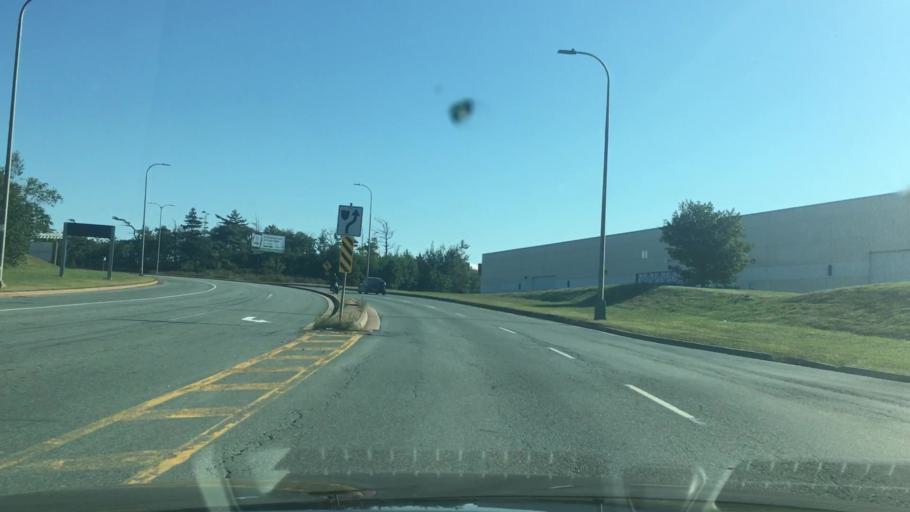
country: CA
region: Nova Scotia
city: Dartmouth
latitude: 44.7177
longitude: -63.5819
